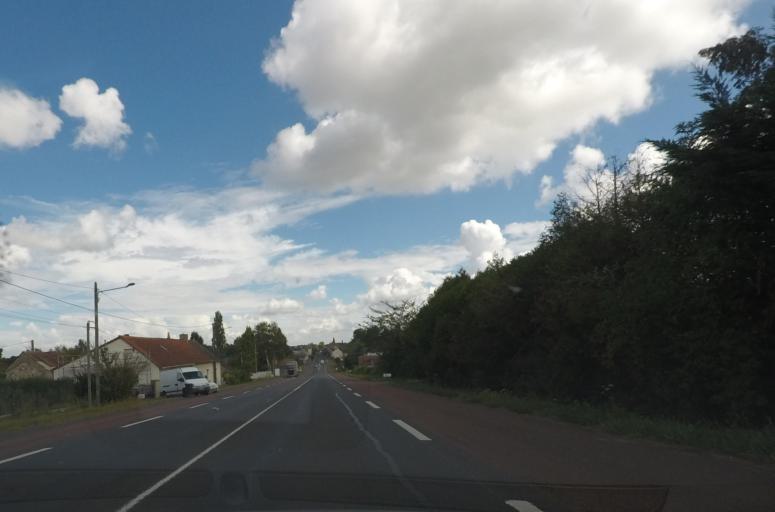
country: FR
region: Pays de la Loire
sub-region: Departement de la Sarthe
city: Cerans-Foulletourte
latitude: 47.8216
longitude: 0.0704
